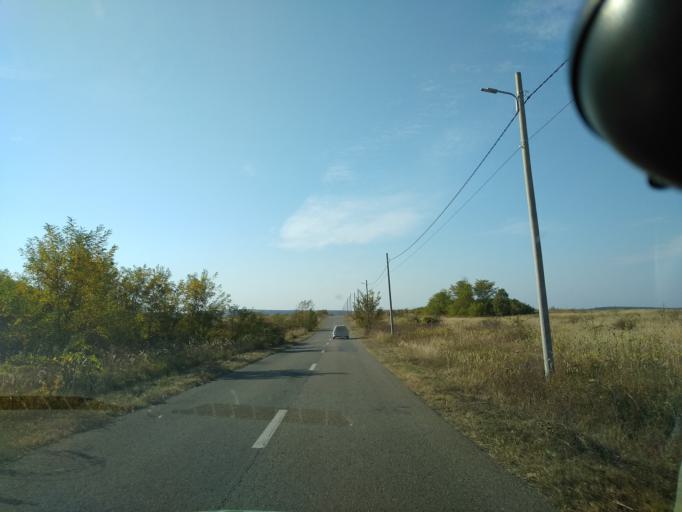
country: RO
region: Timis
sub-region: Oras Recas
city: Recas
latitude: 45.8752
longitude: 21.5181
